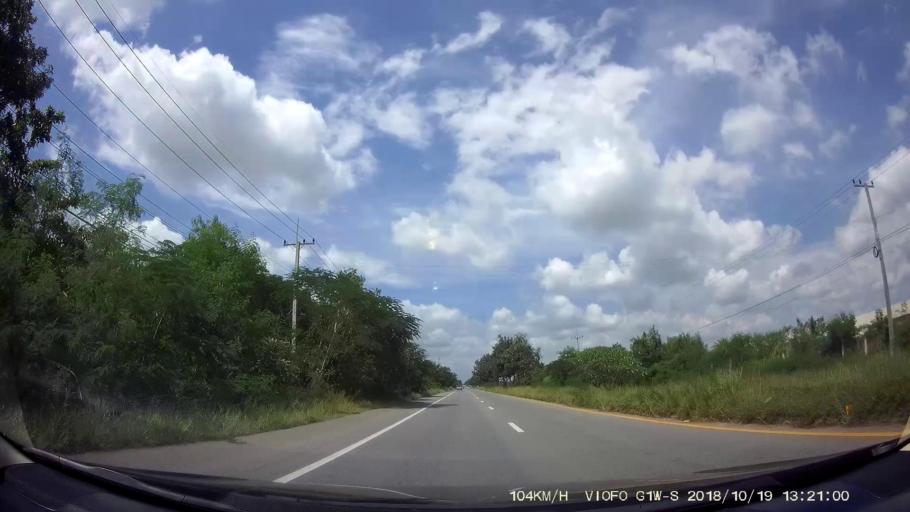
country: TH
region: Chaiyaphum
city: Chatturat
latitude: 15.4547
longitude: 101.8271
